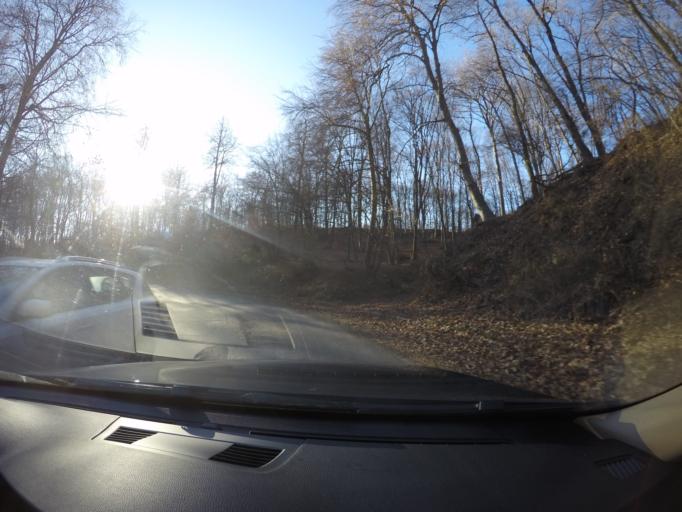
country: HU
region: Pest
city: Visegrad
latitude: 47.7928
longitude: 18.9936
